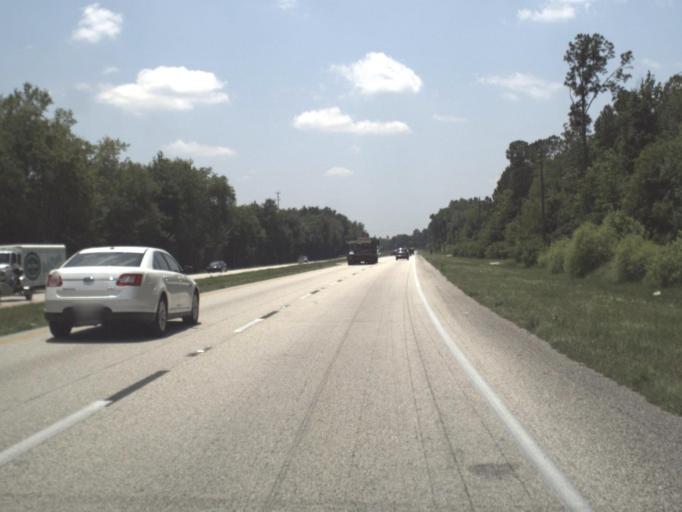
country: US
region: Florida
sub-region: Alachua County
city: Waldo
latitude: 29.8437
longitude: -82.1606
